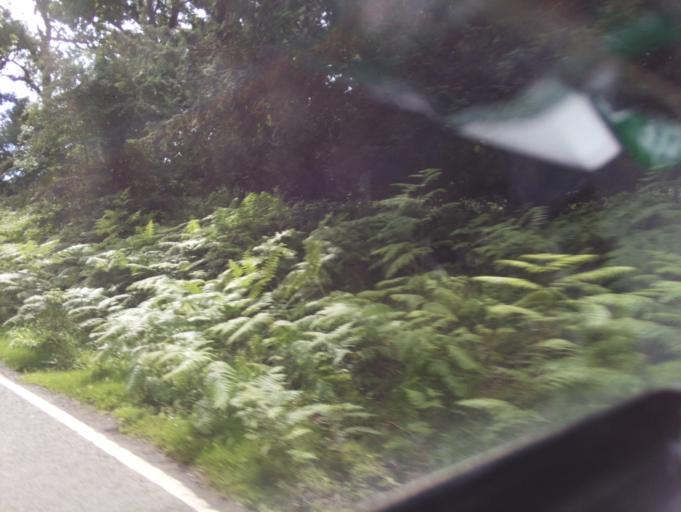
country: GB
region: England
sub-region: Gloucestershire
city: Lydney
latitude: 51.7790
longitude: -2.5308
